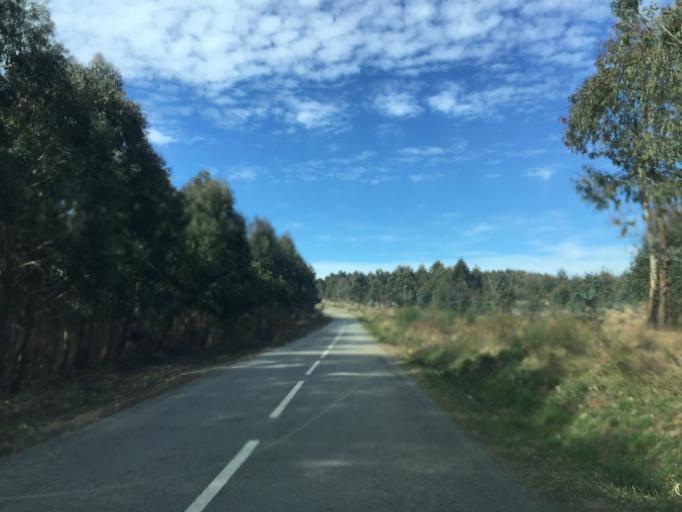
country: PT
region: Aveiro
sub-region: Arouca
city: Arouca
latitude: 40.9616
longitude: -8.2364
